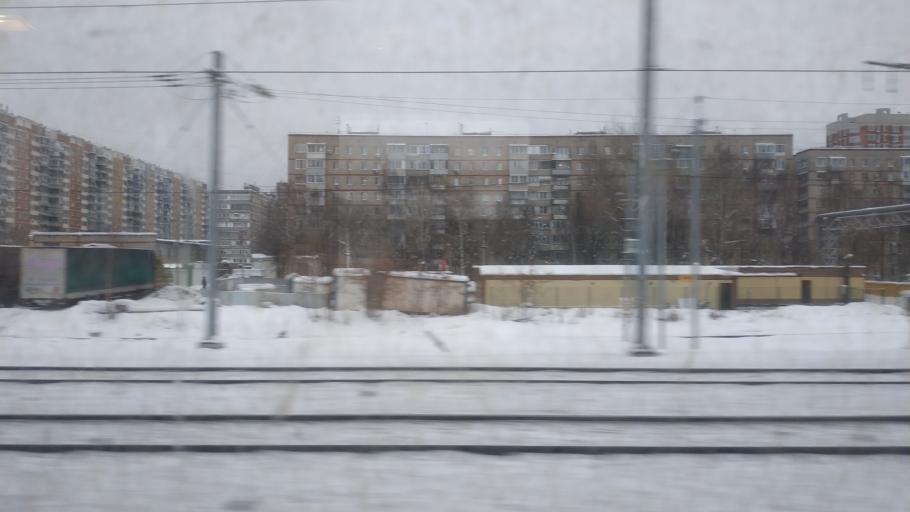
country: RU
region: Moskovskaya
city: Shcherbinka
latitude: 55.5074
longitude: 37.5614
